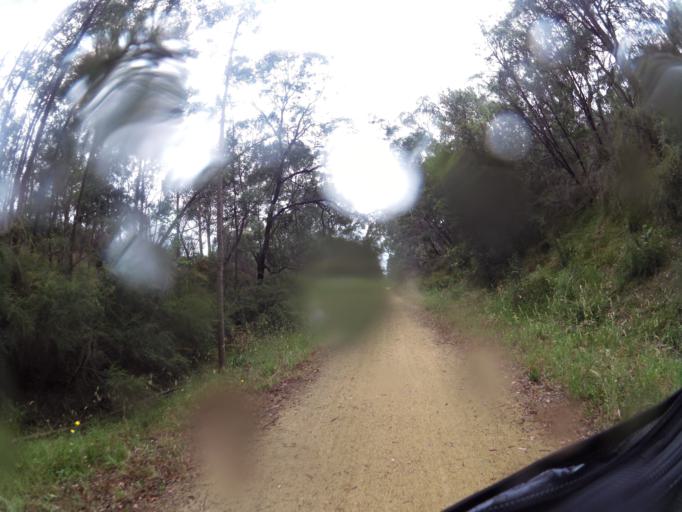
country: AU
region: Victoria
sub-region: East Gippsland
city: Bairnsdale
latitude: -37.7448
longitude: 147.8100
